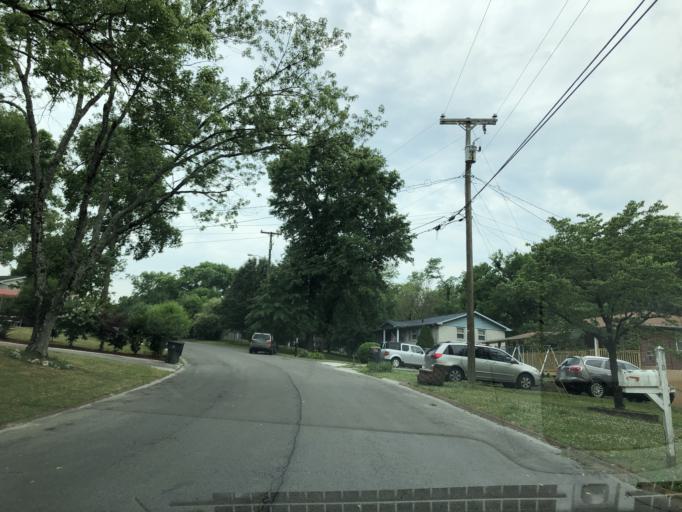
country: US
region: Tennessee
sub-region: Davidson County
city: Oak Hill
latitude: 36.0788
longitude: -86.6867
